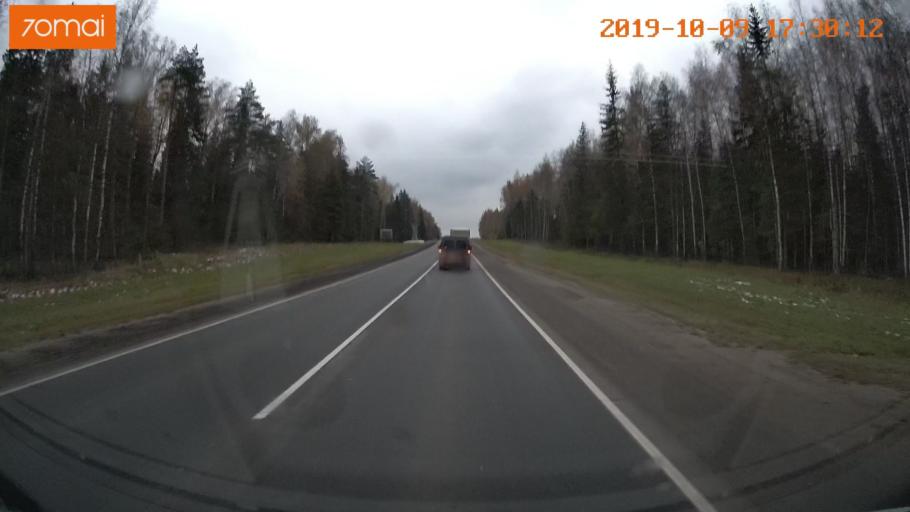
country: RU
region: Ivanovo
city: Bogorodskoye
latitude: 57.1446
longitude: 41.0519
